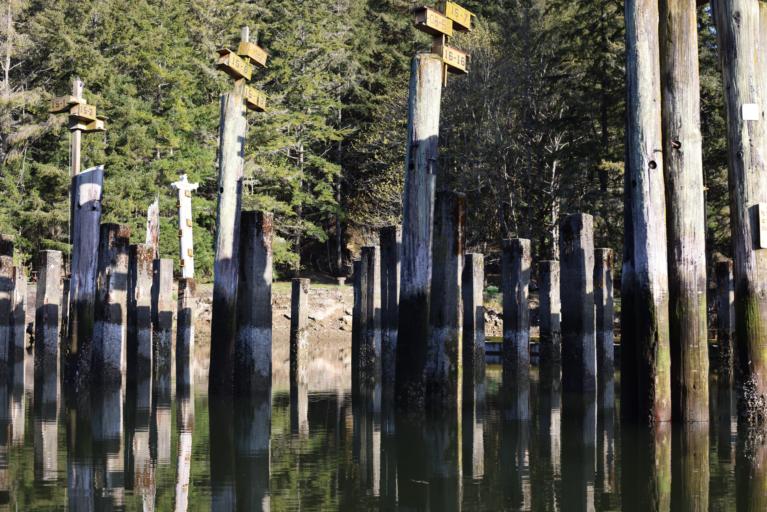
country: CA
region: British Columbia
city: Langford
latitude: 48.5608
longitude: -123.4698
